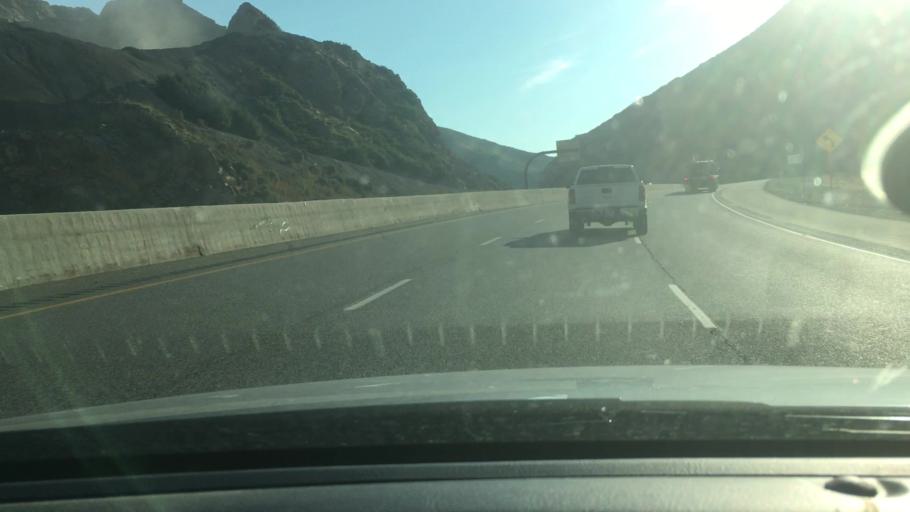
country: US
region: Utah
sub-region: Salt Lake County
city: Mount Olympus
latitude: 40.7254
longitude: -111.7726
